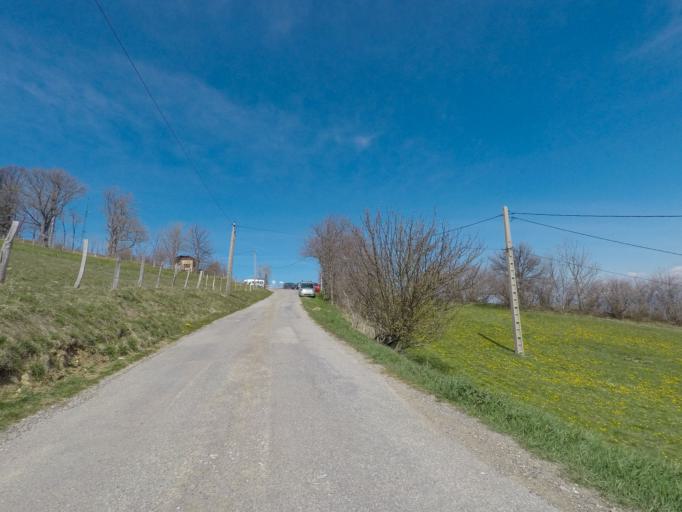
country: FR
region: Rhone-Alpes
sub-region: Departement de la Haute-Savoie
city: Collonges-sous-Saleve
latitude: 46.1271
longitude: 6.1739
